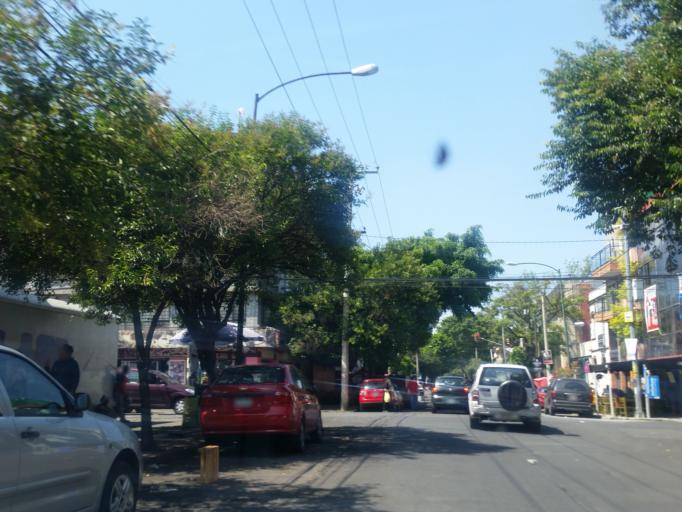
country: MX
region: Mexico City
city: Benito Juarez
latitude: 19.4178
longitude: -99.1571
